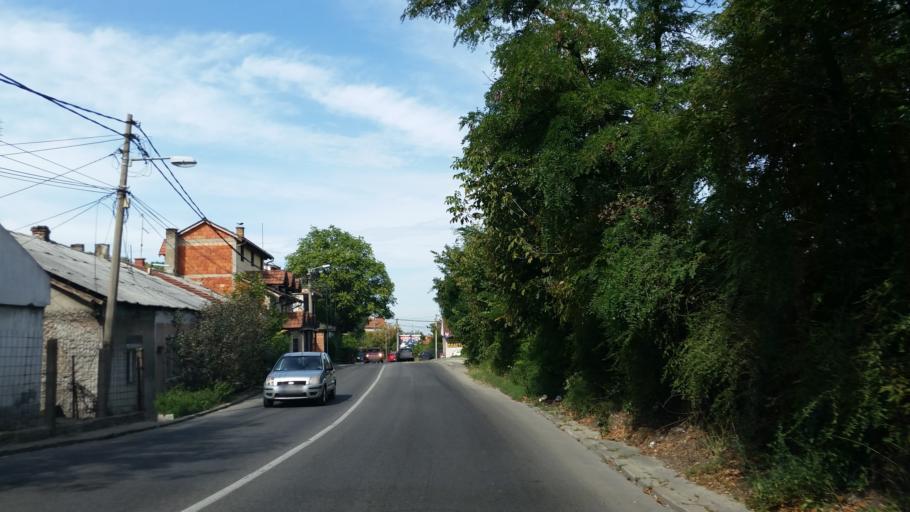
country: RS
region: Central Serbia
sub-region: Belgrade
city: Palilula
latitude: 44.8102
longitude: 20.5109
